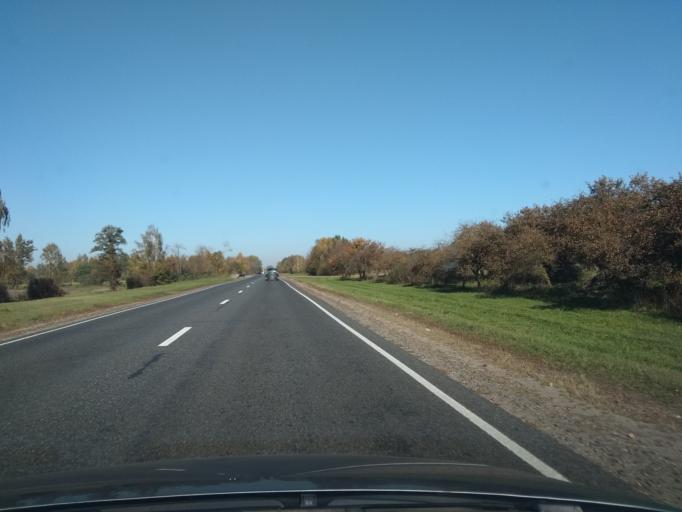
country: BY
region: Brest
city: Kobryn
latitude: 52.1486
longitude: 24.3108
